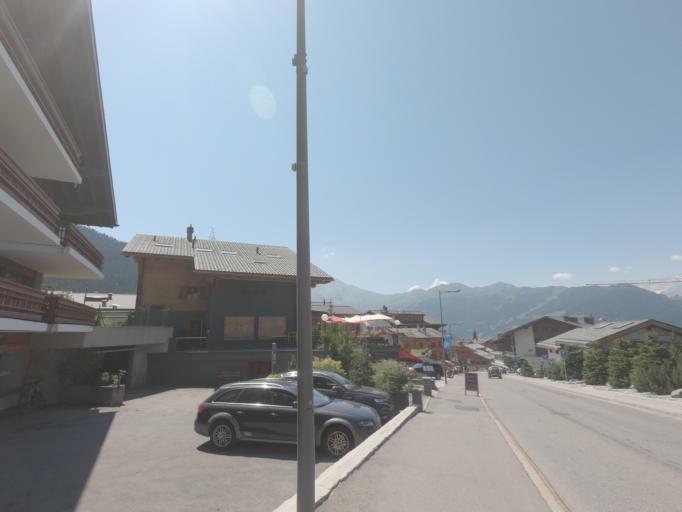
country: CH
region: Valais
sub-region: Entremont District
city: Verbier
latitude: 46.0976
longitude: 7.2297
